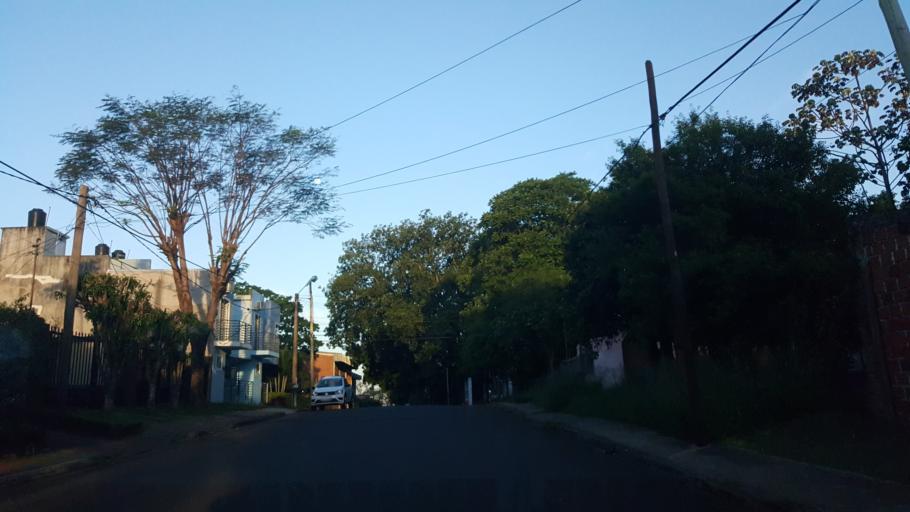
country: AR
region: Misiones
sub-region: Departamento de Capital
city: Posadas
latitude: -27.3820
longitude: -55.9059
